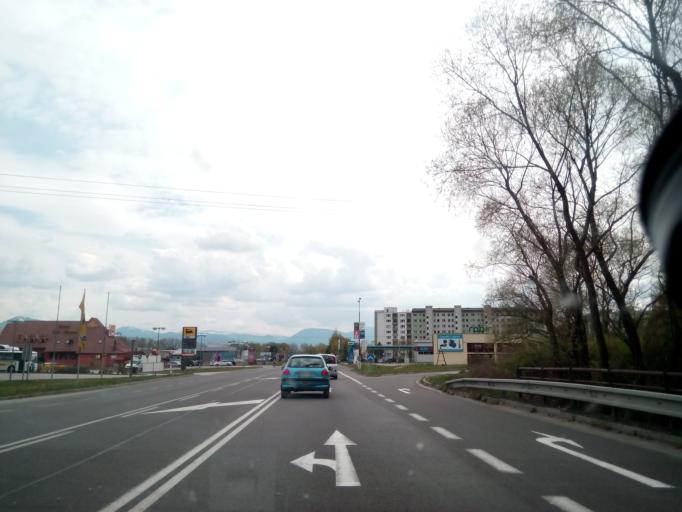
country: SK
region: Zilinsky
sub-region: Okres Zilina
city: Vrutky
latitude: 49.1011
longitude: 18.9193
